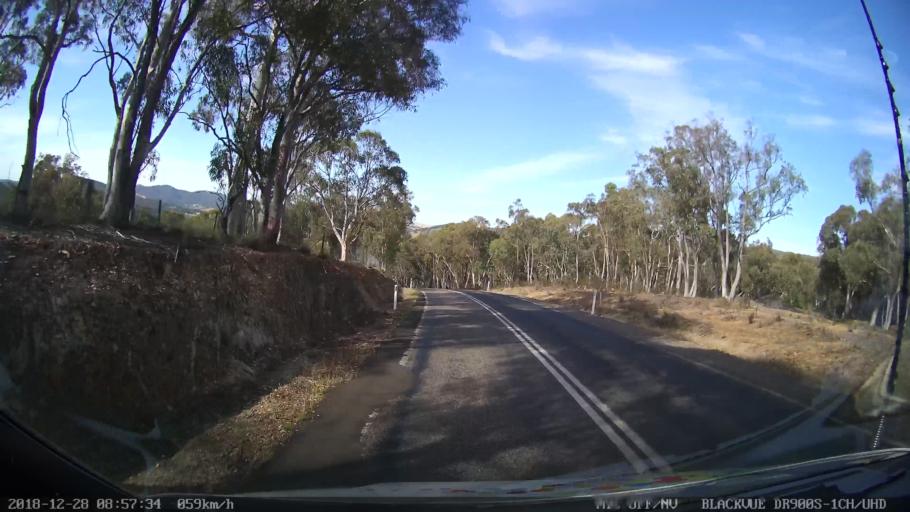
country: AU
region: New South Wales
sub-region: Upper Lachlan Shire
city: Crookwell
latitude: -34.1193
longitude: 149.3343
